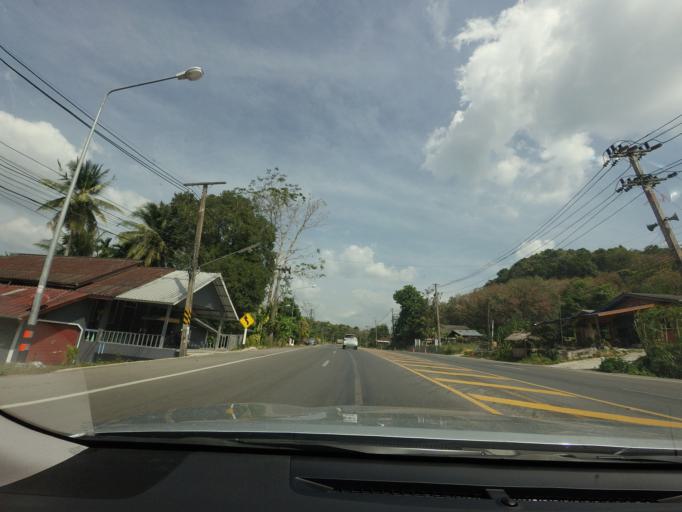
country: TH
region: Phangnga
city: Ban Ao Nang
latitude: 8.0521
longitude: 98.7689
